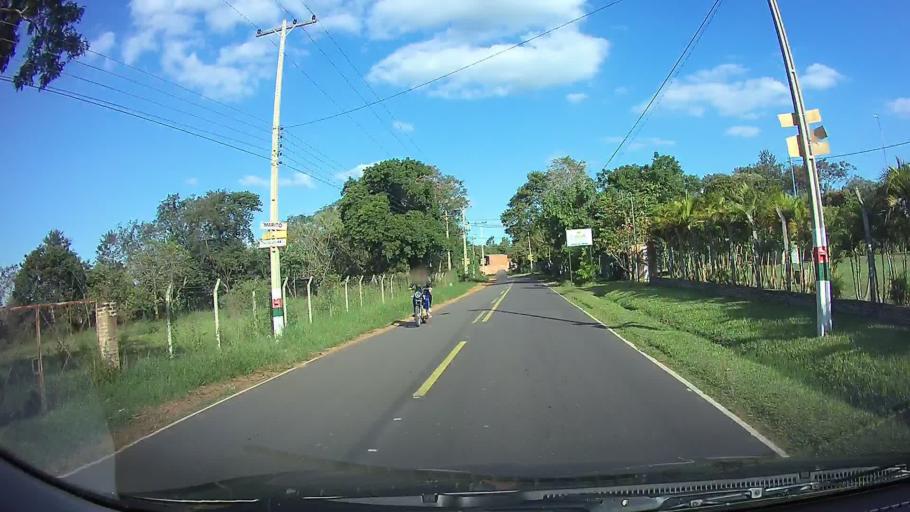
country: PY
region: Central
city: Aregua
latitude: -25.3031
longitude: -57.3892
